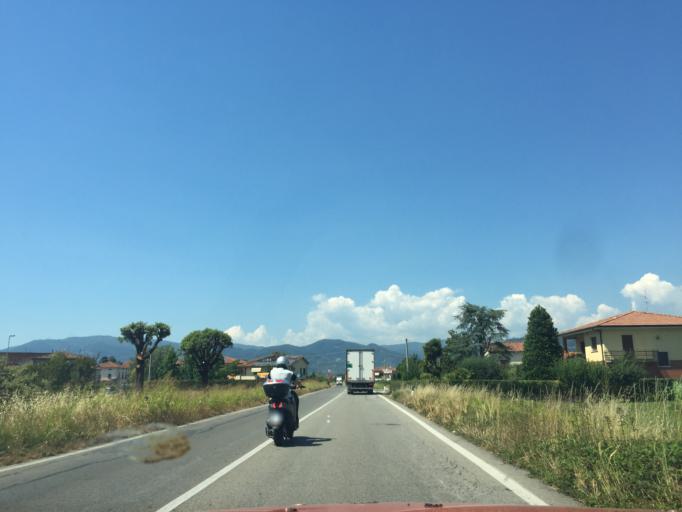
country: IT
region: Tuscany
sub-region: Provincia di Pistoia
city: Chiesina Uzzanese
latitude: 43.8478
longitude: 10.7109
